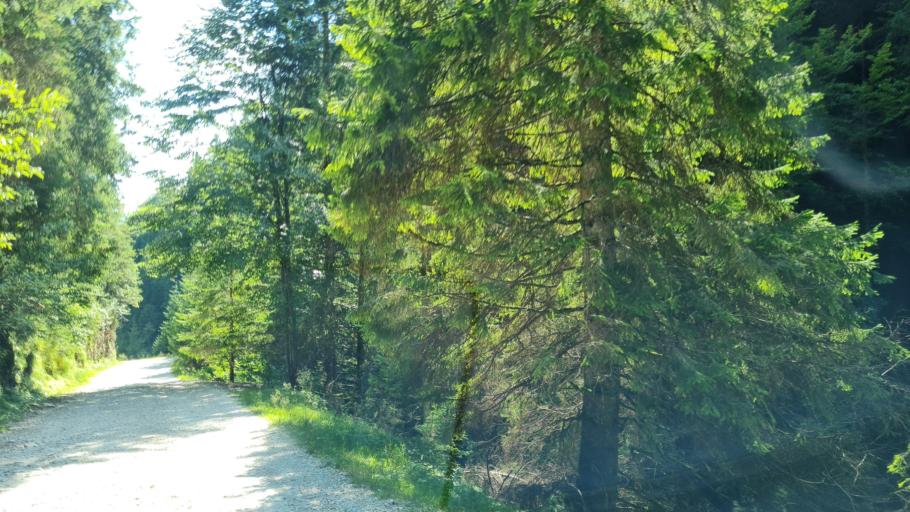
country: IT
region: Veneto
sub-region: Provincia di Vicenza
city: Roana
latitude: 45.9189
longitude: 11.4755
